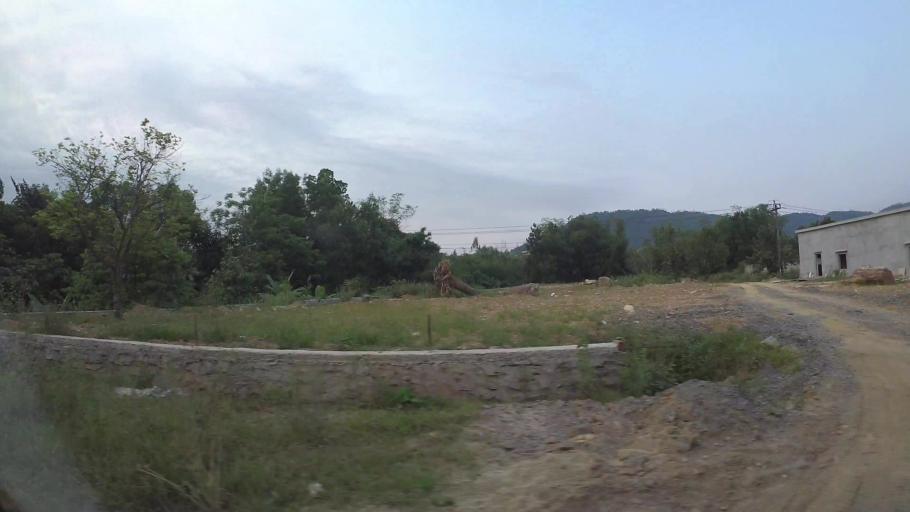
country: VN
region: Da Nang
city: Lien Chieu
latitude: 16.0530
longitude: 108.1109
